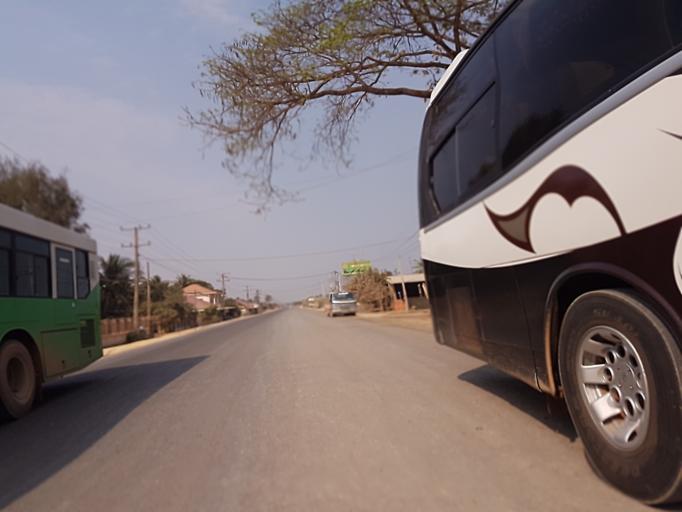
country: TH
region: Nong Khai
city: Nong Khai
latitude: 17.9138
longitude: 102.7647
